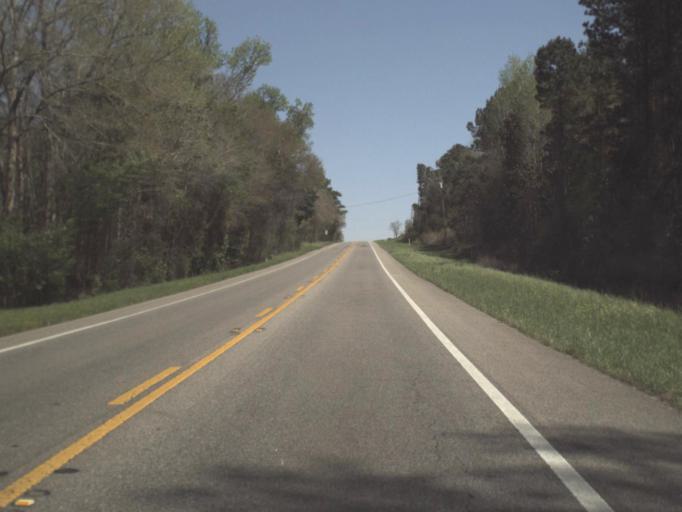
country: US
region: Florida
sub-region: Calhoun County
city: Blountstown
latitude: 30.4261
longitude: -85.1589
